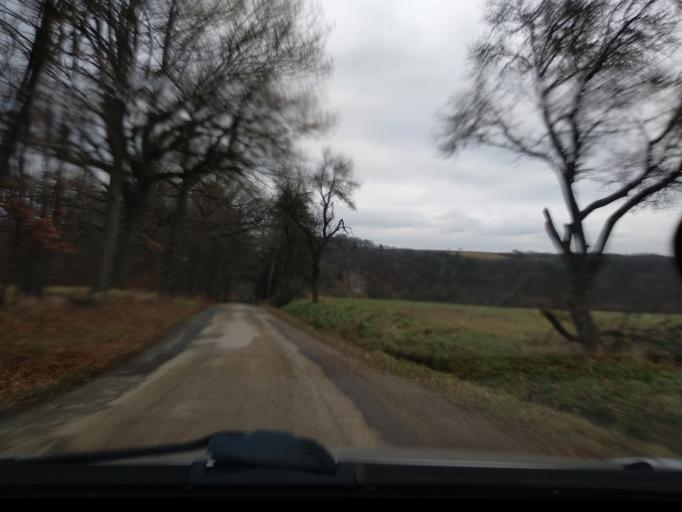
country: CZ
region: South Moravian
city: Lysice
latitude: 49.3935
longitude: 16.5223
